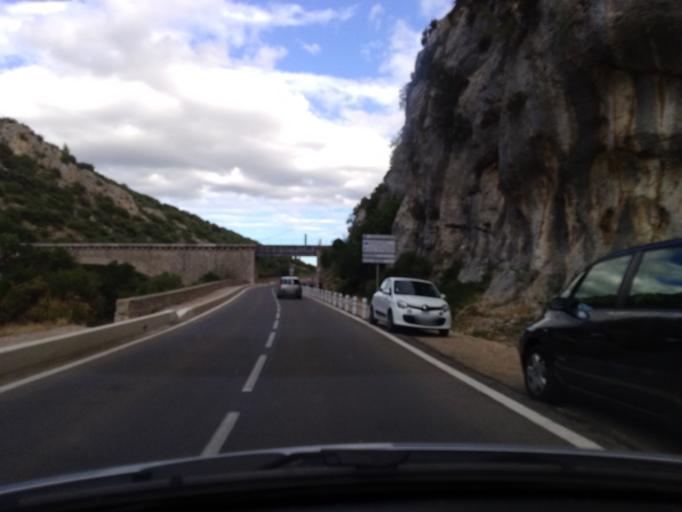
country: FR
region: Languedoc-Roussillon
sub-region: Departement de l'Herault
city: Saint-Jean-de-Fos
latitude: 43.7093
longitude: 3.5545
